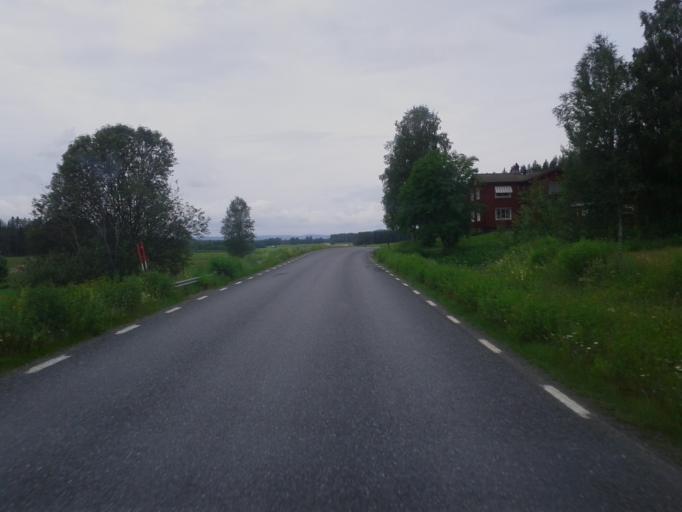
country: SE
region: Vaesterbotten
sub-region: Skelleftea Kommun
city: Viken
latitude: 64.8885
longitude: 20.7459
